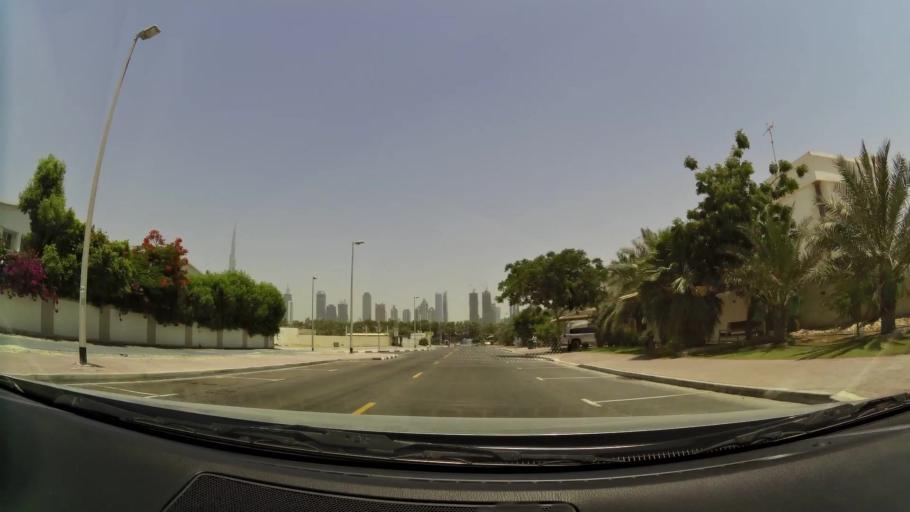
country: AE
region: Dubai
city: Dubai
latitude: 25.1980
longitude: 55.2448
